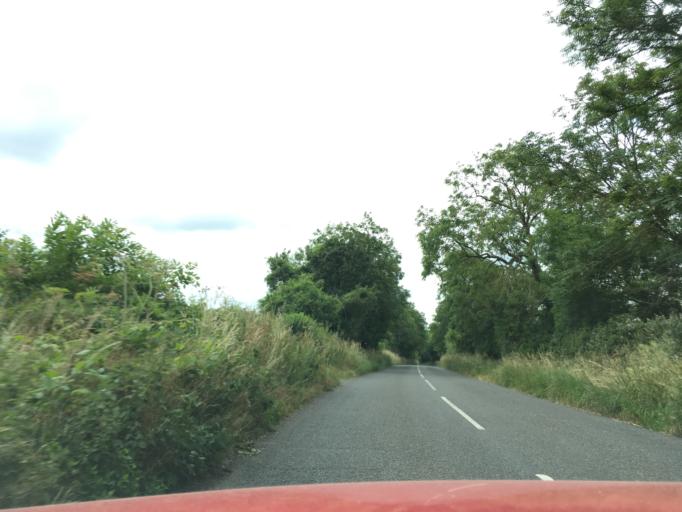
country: GB
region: England
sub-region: Oxfordshire
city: Charlbury
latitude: 51.8998
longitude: -1.4908
